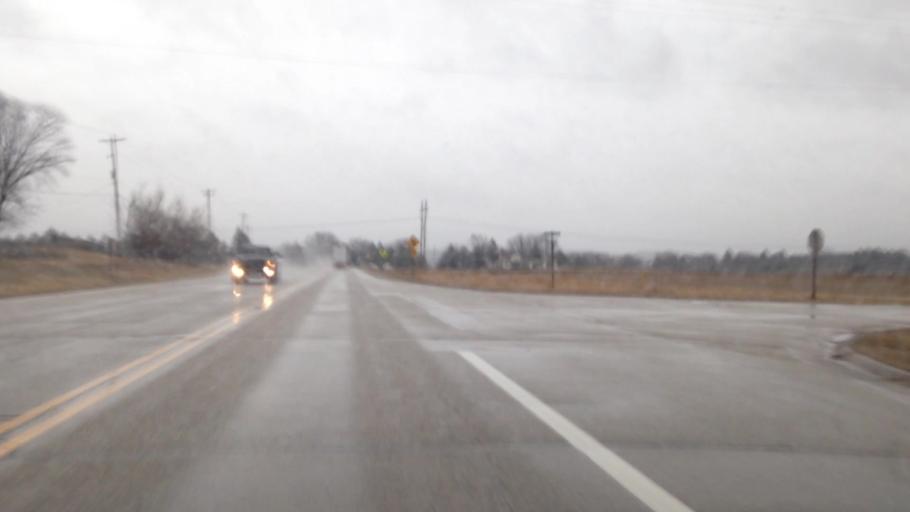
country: US
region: Wisconsin
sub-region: Washington County
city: Hartford
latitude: 43.4213
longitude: -88.3614
